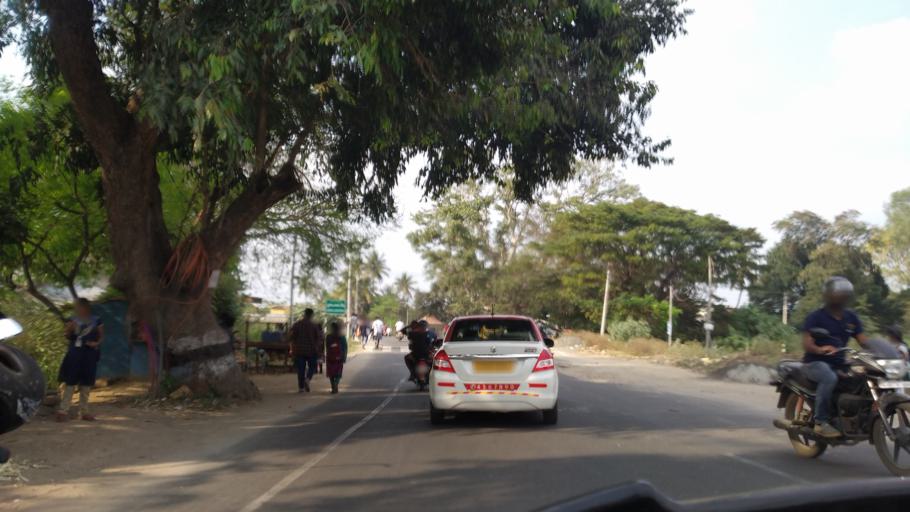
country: IN
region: Tamil Nadu
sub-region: Coimbatore
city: Perur
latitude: 10.9816
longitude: 76.9215
